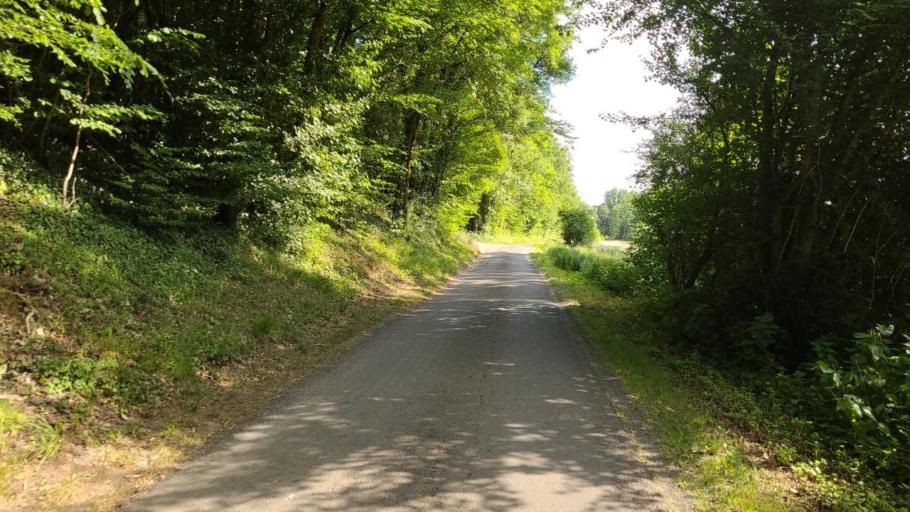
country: FR
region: Centre
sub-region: Departement d'Indre-et-Loire
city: Reugny
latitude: 47.4753
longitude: 0.8885
